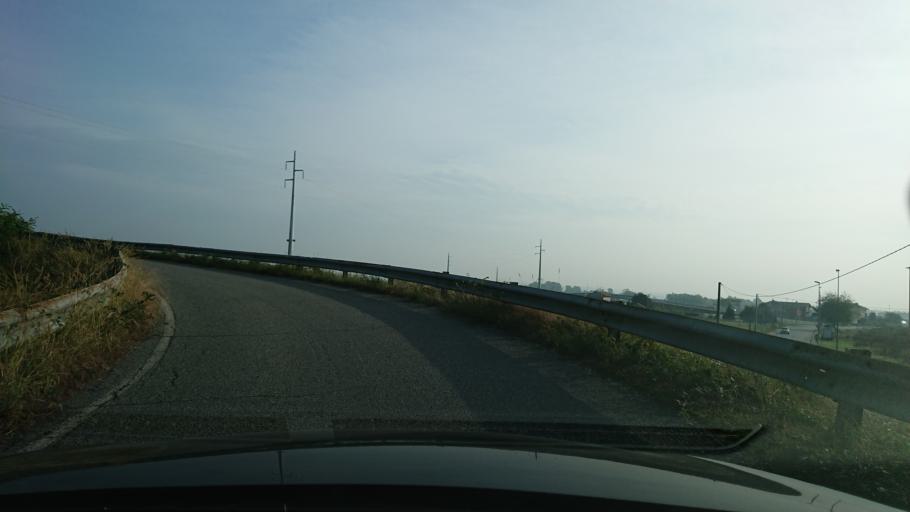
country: IT
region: Piedmont
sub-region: Provincia di Biella
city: Valdengo
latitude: 45.5544
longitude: 8.1341
